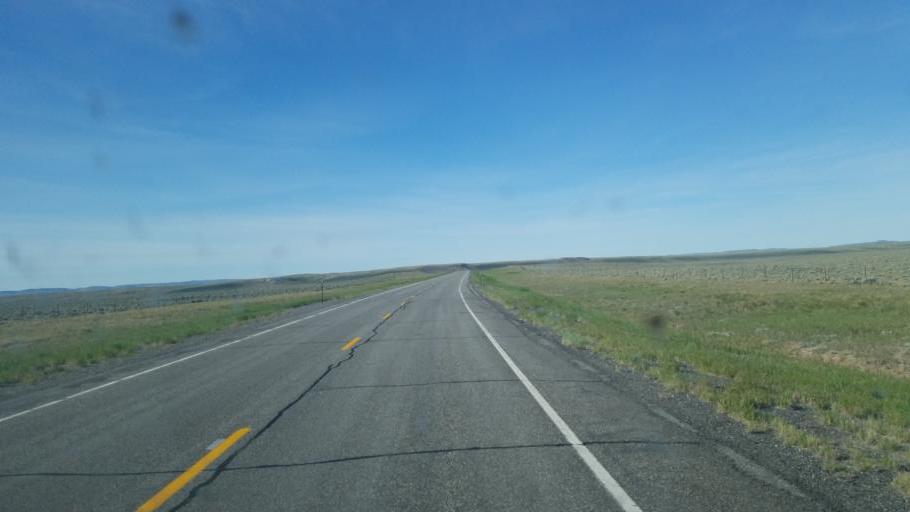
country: US
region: Wyoming
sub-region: Fremont County
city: Riverton
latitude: 42.6351
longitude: -108.1939
